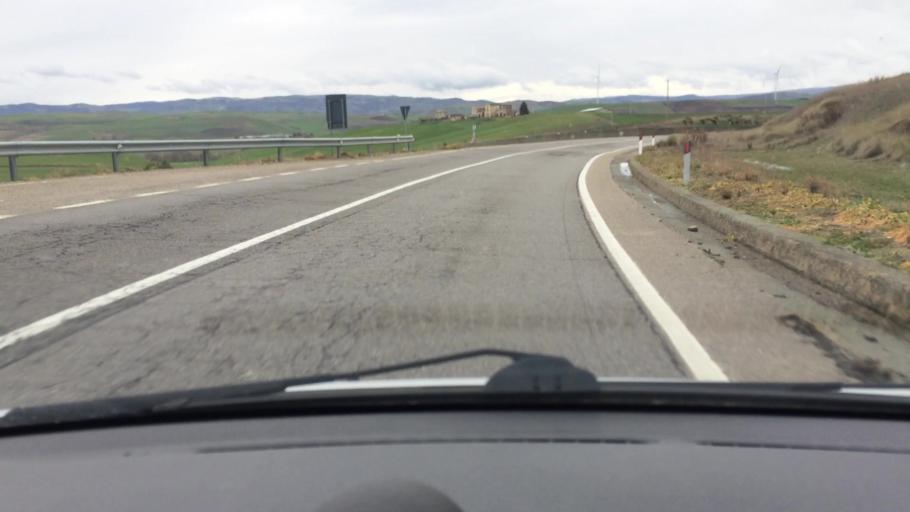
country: IT
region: Basilicate
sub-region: Provincia di Potenza
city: San Chirico Nuovo
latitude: 40.7758
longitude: 16.1300
